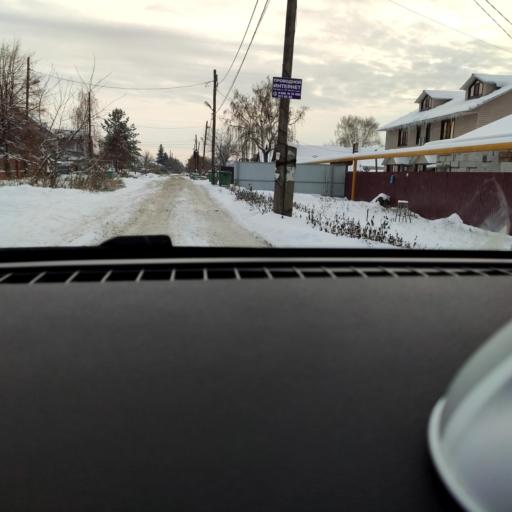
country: RU
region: Samara
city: Petra-Dubrava
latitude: 53.2534
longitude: 50.3435
